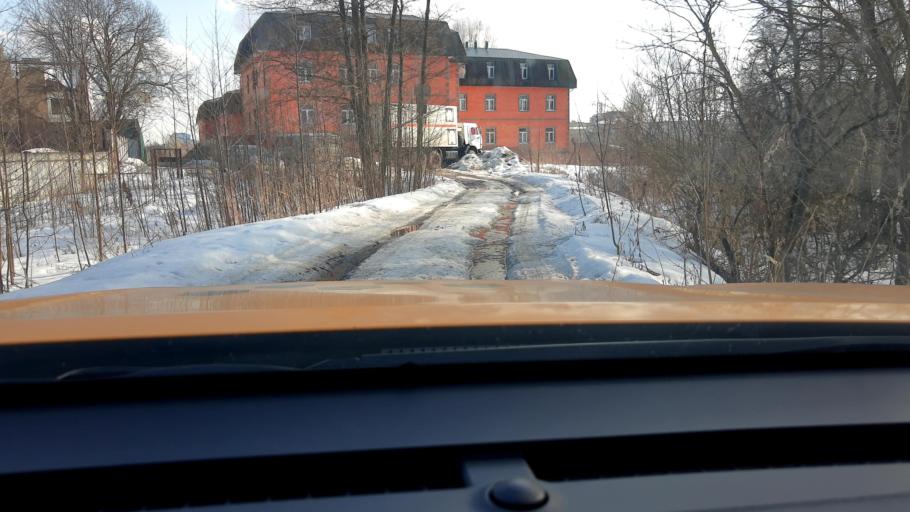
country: RU
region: Moskovskaya
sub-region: Leninskiy Rayon
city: Vnukovo
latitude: 55.6282
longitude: 37.2706
